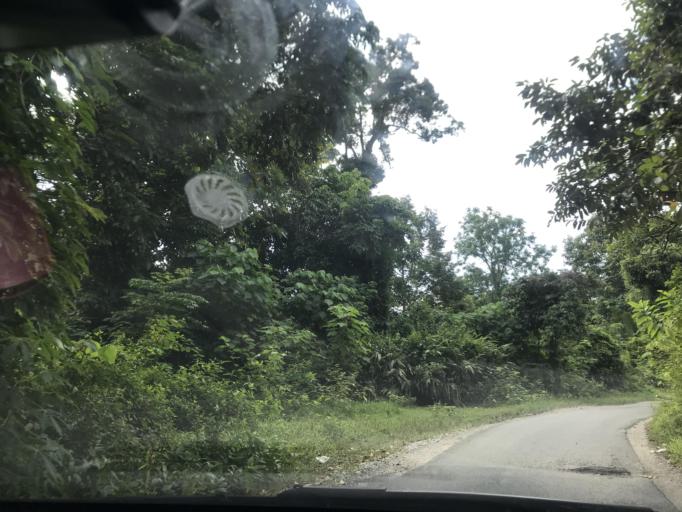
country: MY
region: Kelantan
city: Kota Bharu
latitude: 6.1134
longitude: 102.1801
